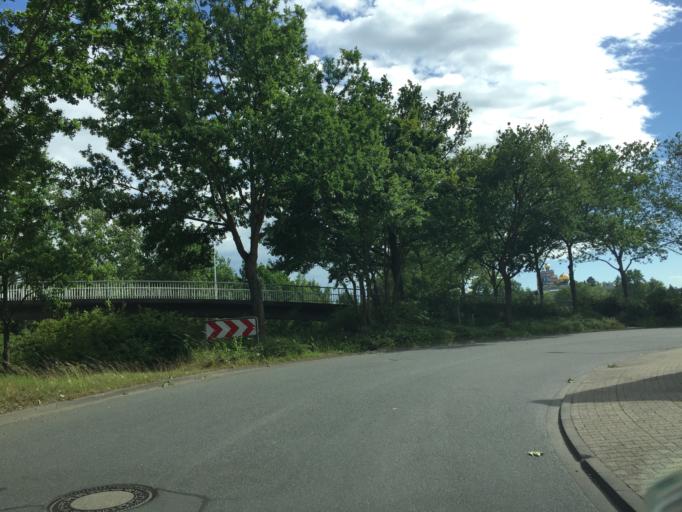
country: DE
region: Hesse
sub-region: Regierungsbezirk Darmstadt
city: Darmstadt
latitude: 49.8886
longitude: 8.6601
